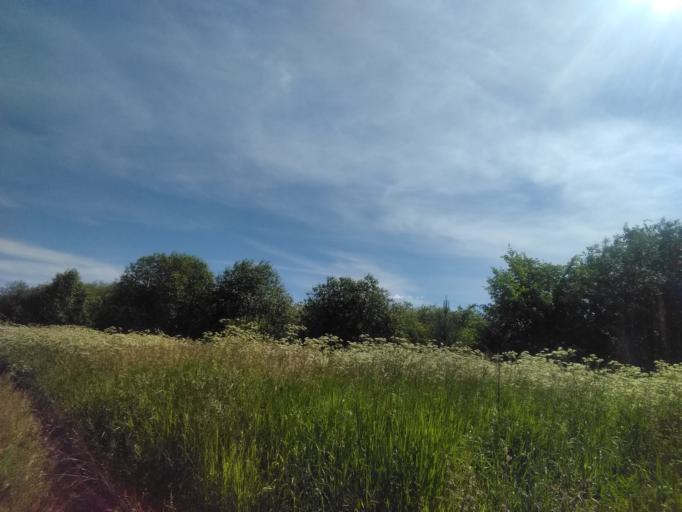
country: RU
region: Udmurtiya
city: Khokhryaki
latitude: 56.8548
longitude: 53.4089
